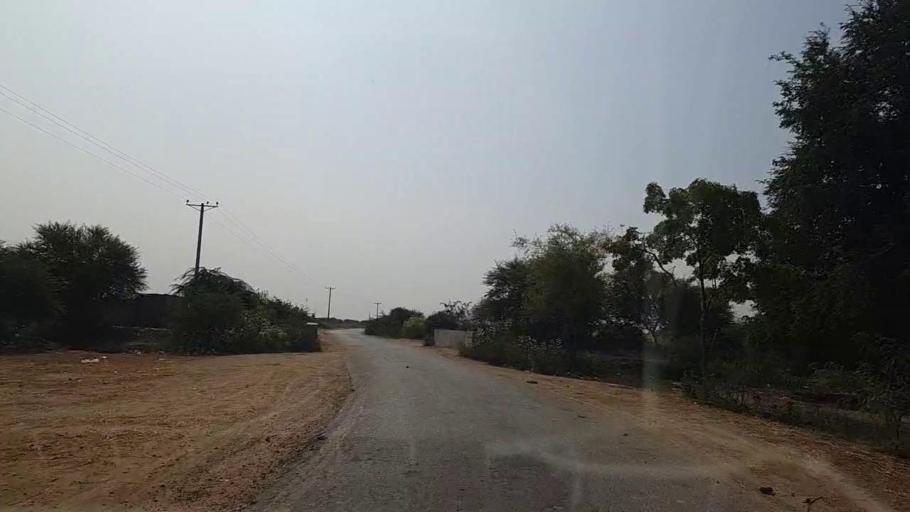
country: PK
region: Sindh
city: Chuhar Jamali
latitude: 24.3467
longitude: 67.9507
